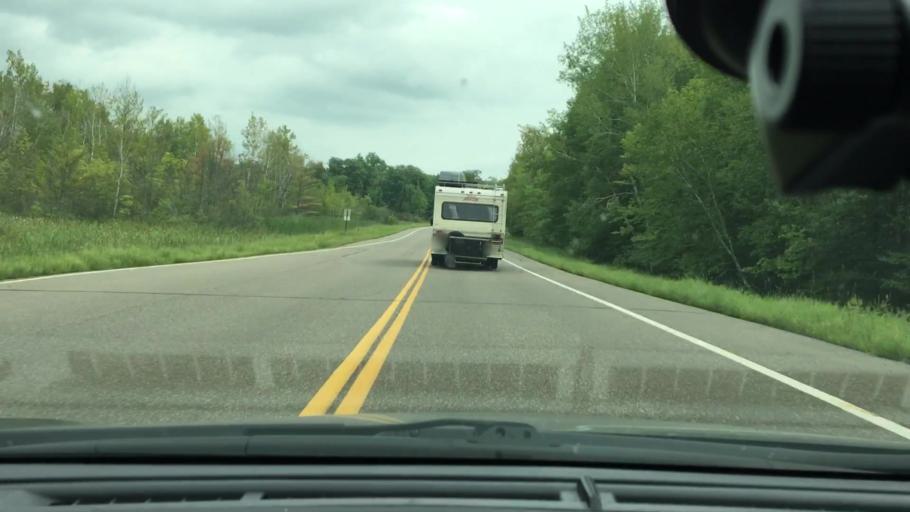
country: US
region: Minnesota
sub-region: Crow Wing County
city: Crosby
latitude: 46.4105
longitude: -93.8346
